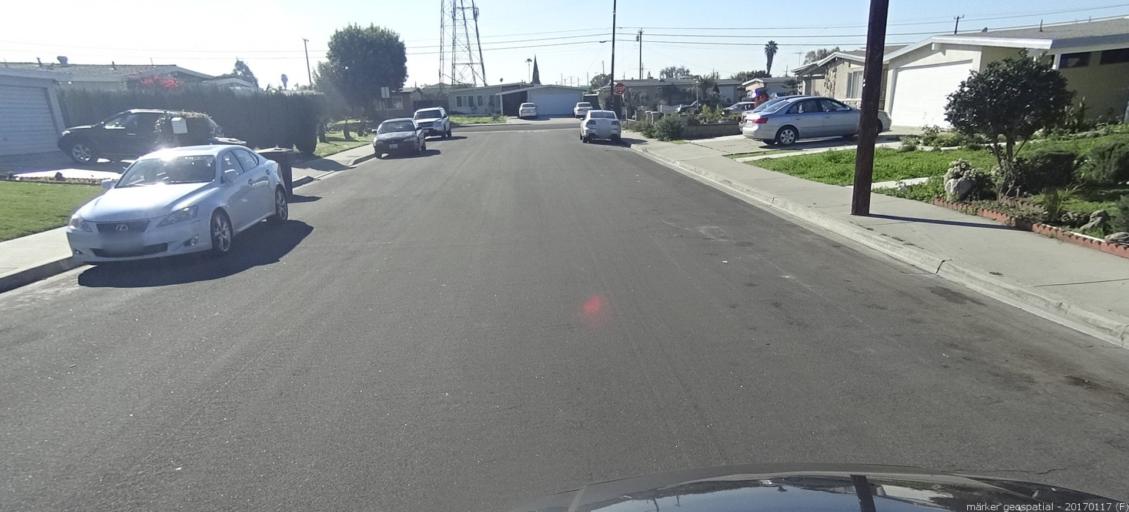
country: US
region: California
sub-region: Orange County
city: Stanton
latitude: 33.8083
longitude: -117.9686
